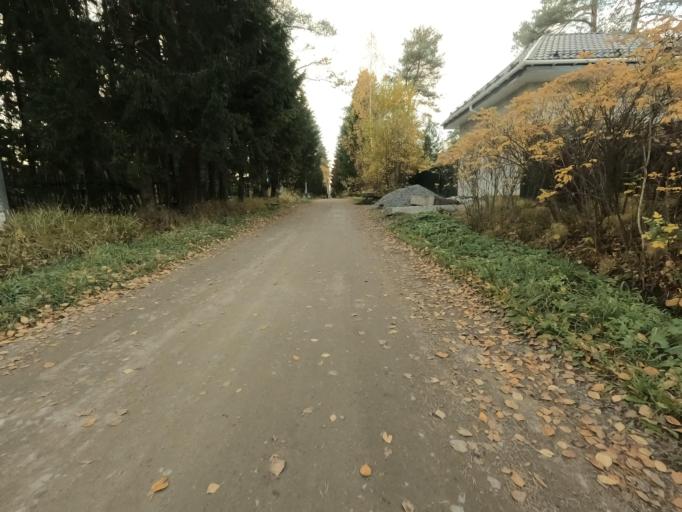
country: RU
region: St.-Petersburg
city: Beloostrov
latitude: 60.1663
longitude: 29.9925
